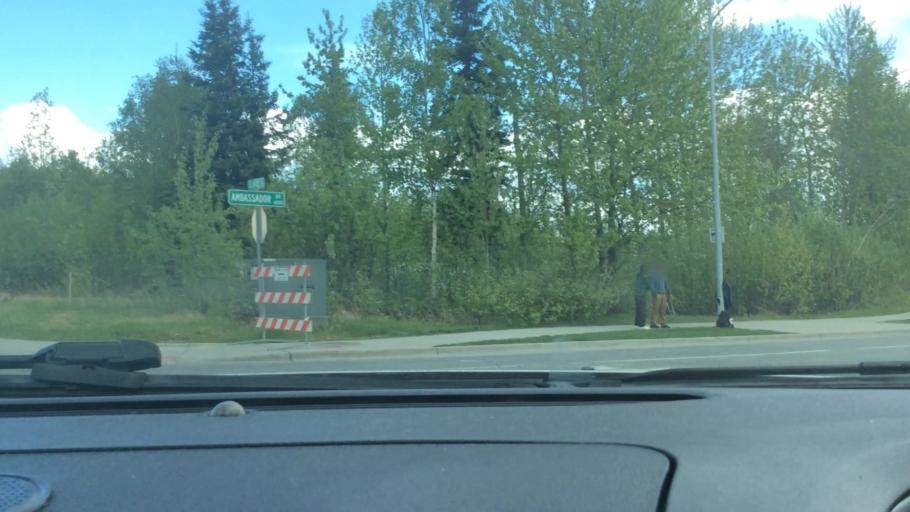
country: US
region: Alaska
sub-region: Anchorage Municipality
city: Anchorage
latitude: 61.1832
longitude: -149.8079
